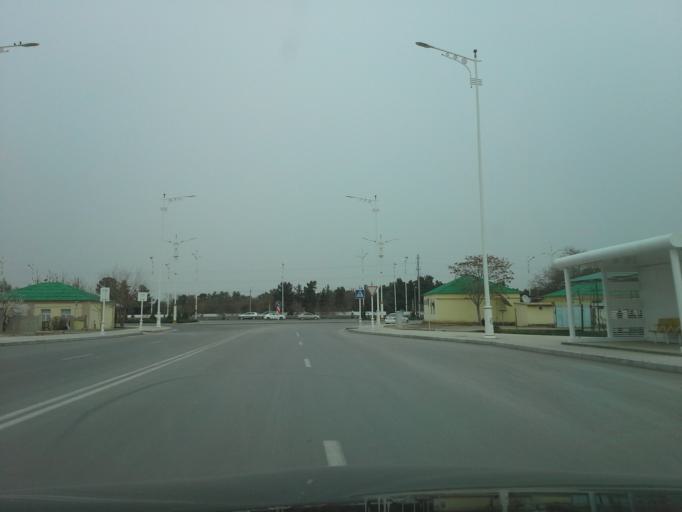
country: TM
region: Ahal
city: Ashgabat
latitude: 37.9696
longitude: 58.3509
